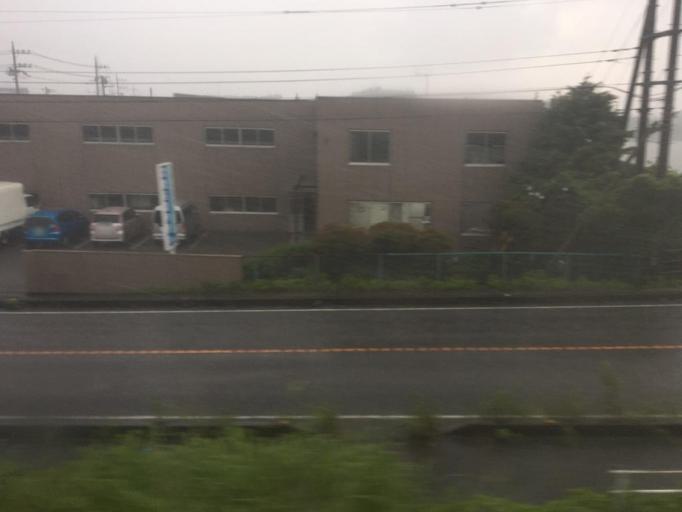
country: JP
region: Gunma
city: Tatebayashi
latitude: 36.2680
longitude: 139.5096
